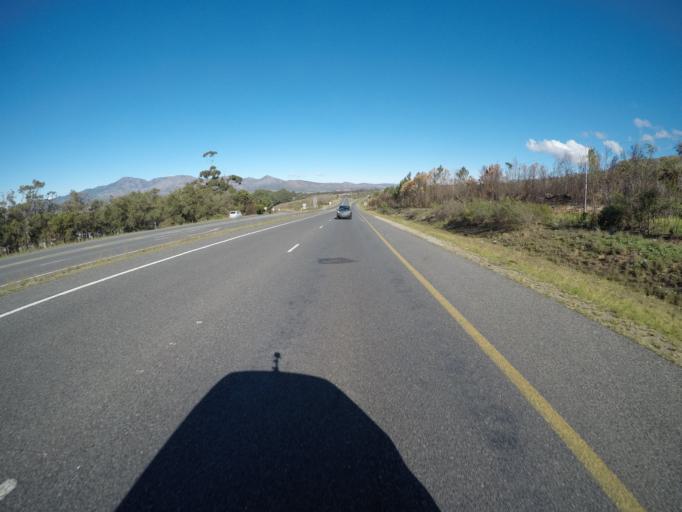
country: ZA
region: Western Cape
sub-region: Overberg District Municipality
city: Grabouw
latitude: -34.2245
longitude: 19.1877
